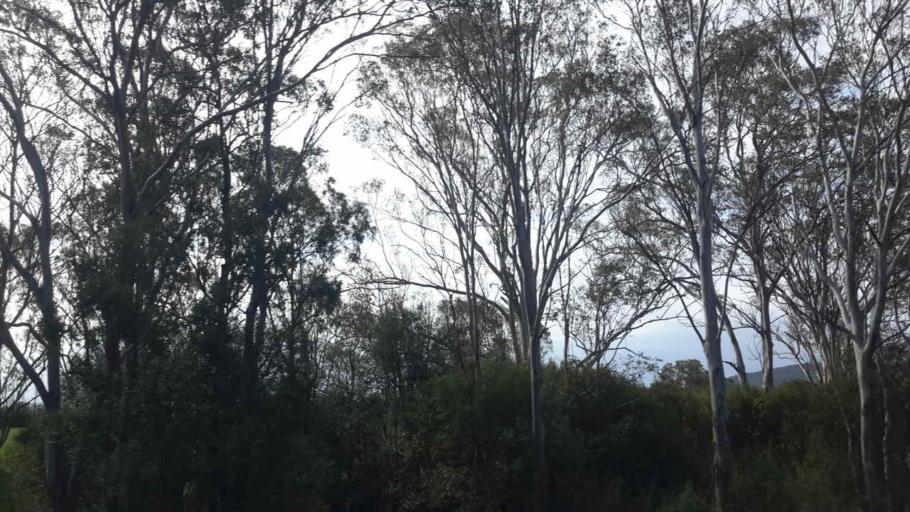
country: AU
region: New South Wales
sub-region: Campbelltown Municipality
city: Glen Alpine
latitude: -34.1073
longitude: 150.7610
